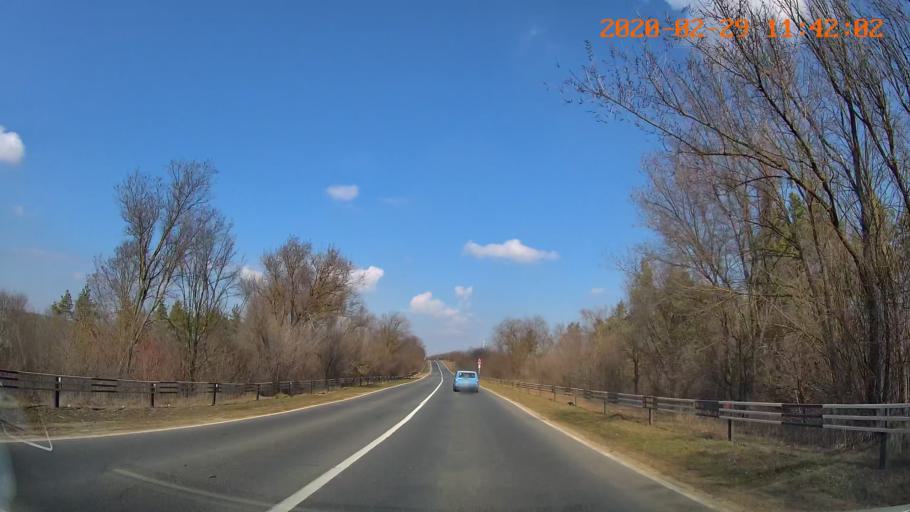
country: MD
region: Rezina
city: Saharna
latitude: 47.6789
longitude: 29.0146
